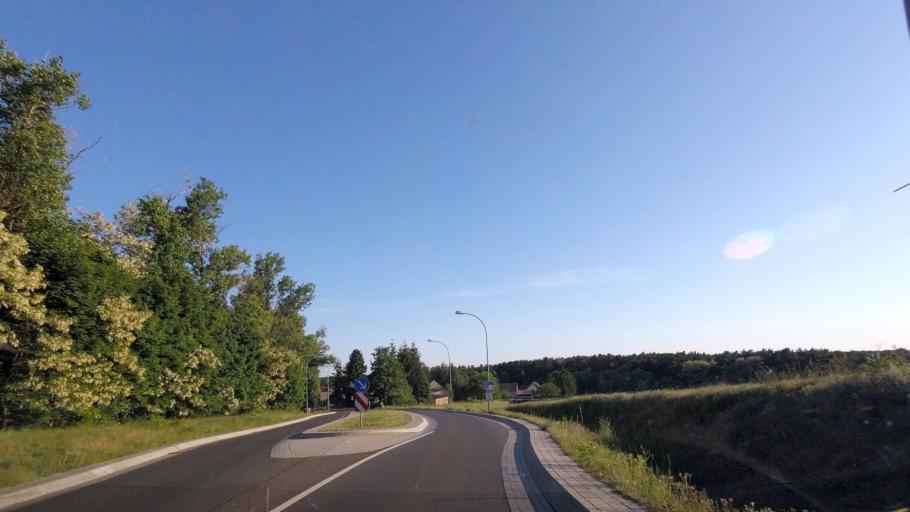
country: DE
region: Brandenburg
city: Golzow
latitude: 52.2937
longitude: 12.6016
